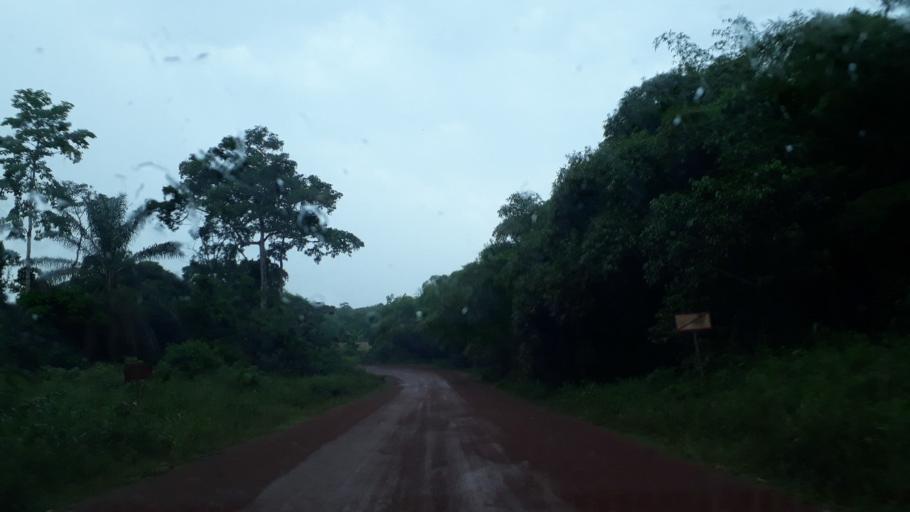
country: CD
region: Eastern Province
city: Kisangani
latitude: 0.4691
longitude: 25.5247
